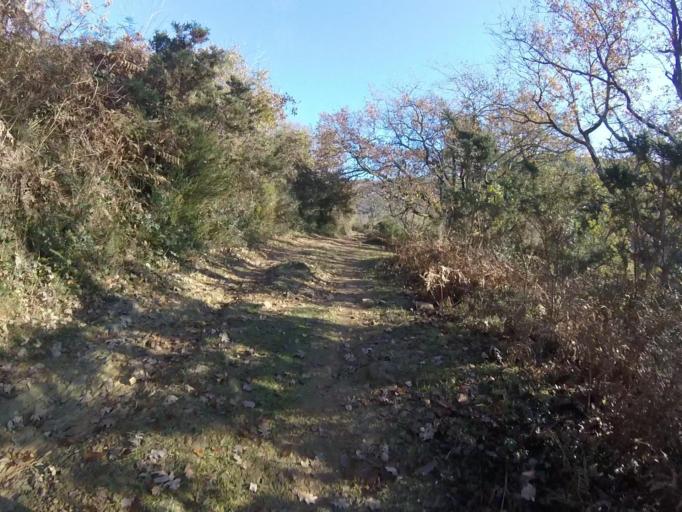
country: ES
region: Navarre
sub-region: Provincia de Navarra
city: Bera
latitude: 43.3140
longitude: -1.7260
